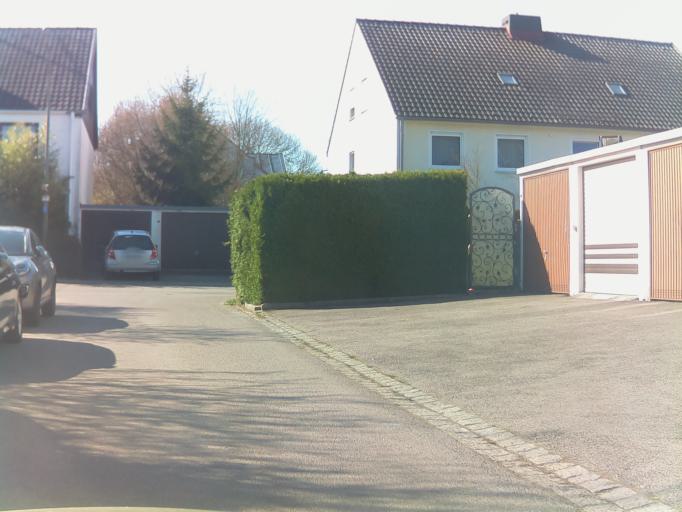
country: DE
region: Bavaria
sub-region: Swabia
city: Stadtbergen
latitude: 48.3648
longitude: 10.8384
